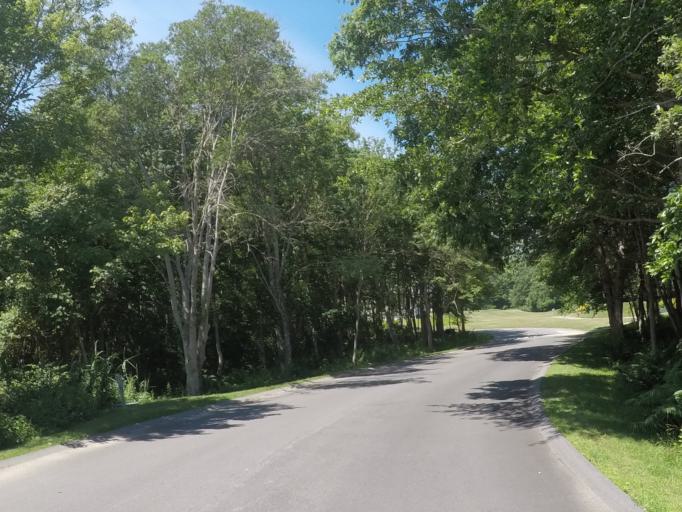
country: US
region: Massachusetts
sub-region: Bristol County
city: Bliss Corner
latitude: 41.5453
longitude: -70.9430
